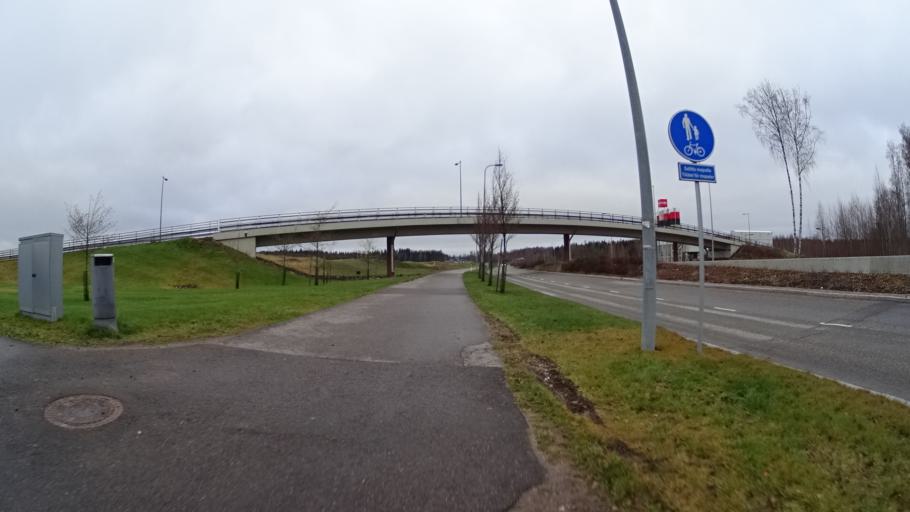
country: FI
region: Uusimaa
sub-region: Helsinki
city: Kilo
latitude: 60.1971
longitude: 24.7878
